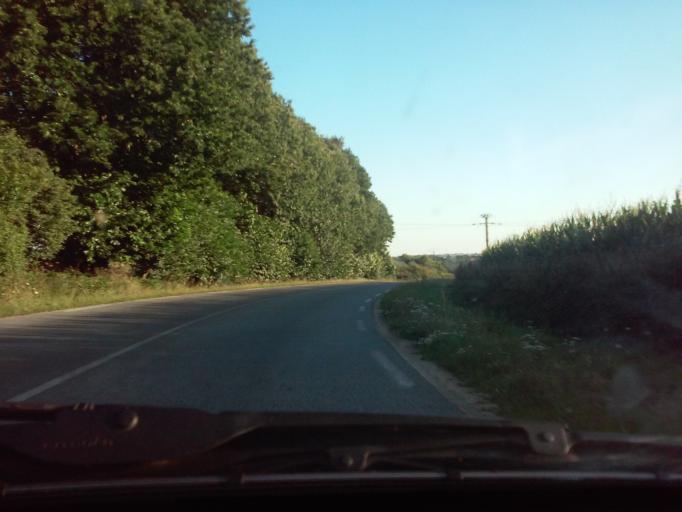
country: FR
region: Brittany
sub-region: Departement des Cotes-d'Armor
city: Saint-Samson-sur-Rance
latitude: 48.4857
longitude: -2.0420
